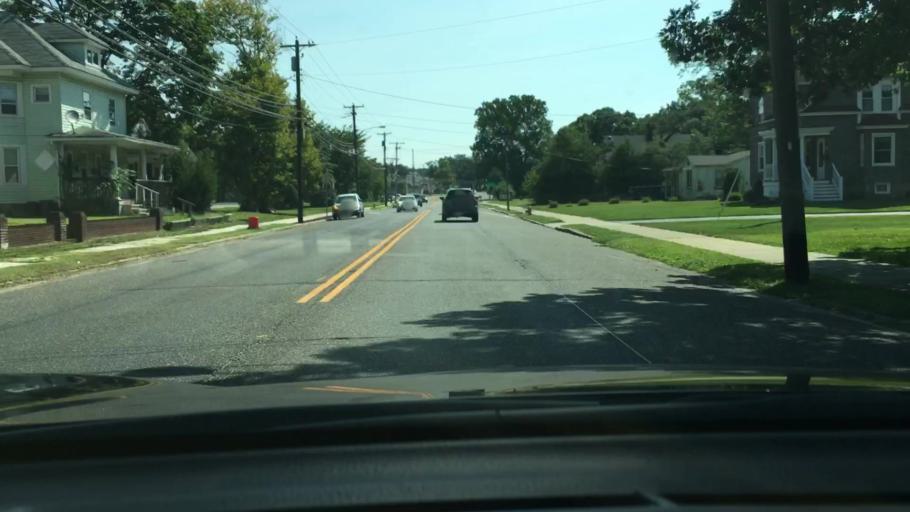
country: US
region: New Jersey
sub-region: Cumberland County
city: Millville
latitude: 39.3949
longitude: -75.0225
